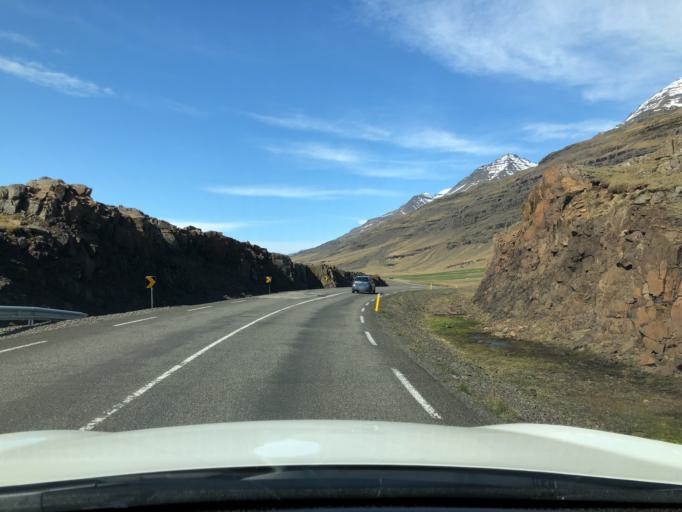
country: IS
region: East
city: Reydarfjoerdur
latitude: 64.5892
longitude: -14.5359
